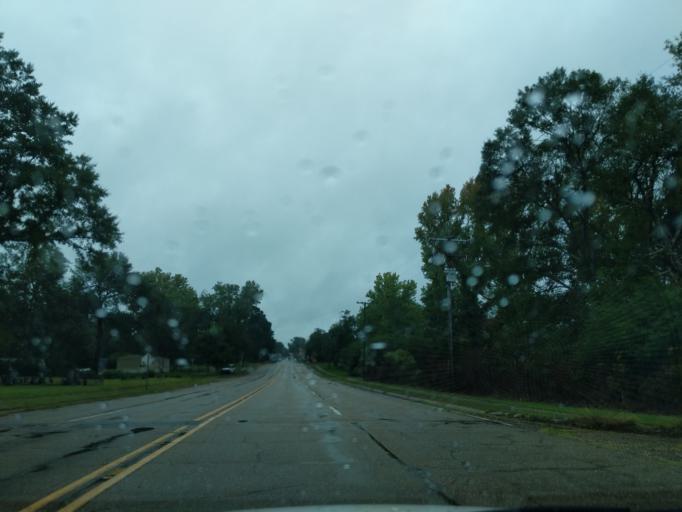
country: US
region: Louisiana
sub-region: Bienville Parish
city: Arcadia
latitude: 32.5499
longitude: -93.0529
